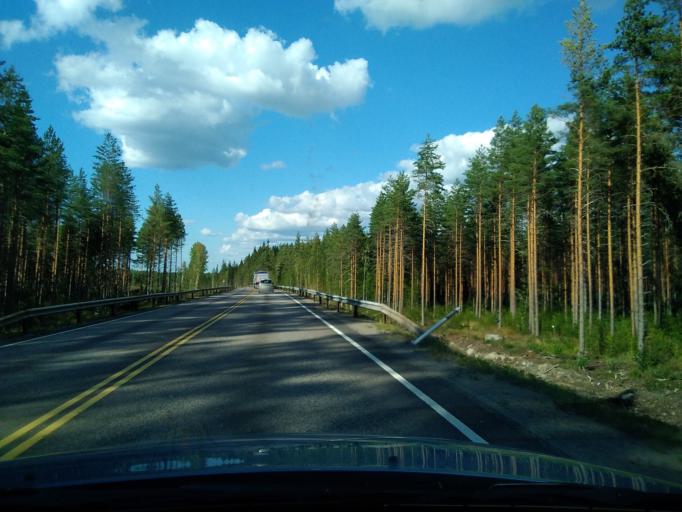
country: FI
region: Central Finland
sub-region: Keuruu
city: Keuruu
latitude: 62.1494
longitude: 24.7494
